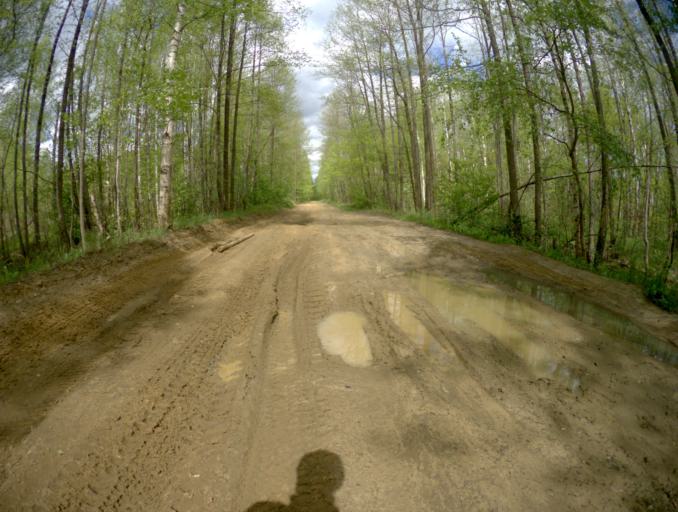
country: RU
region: Moskovskaya
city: Cherusti
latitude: 55.5057
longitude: 40.0203
